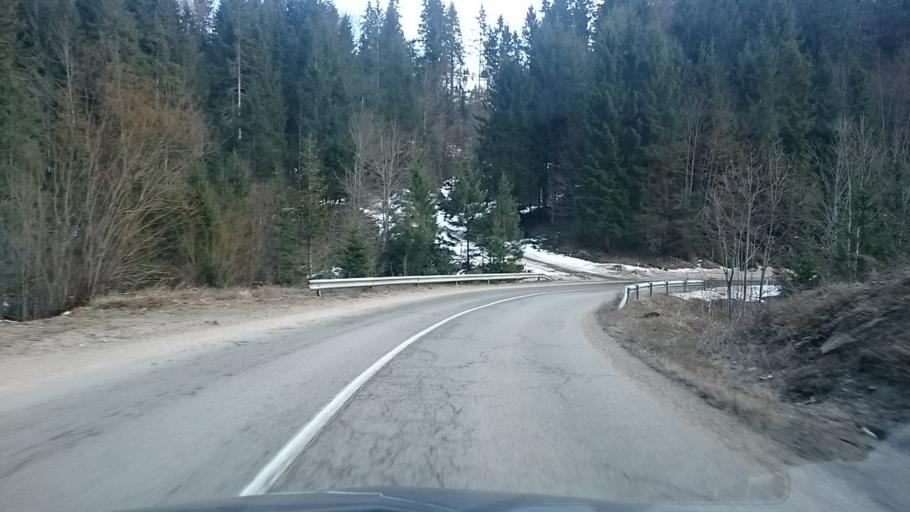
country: BA
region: Republika Srpska
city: Skender Vakuf
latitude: 44.4768
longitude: 17.3920
